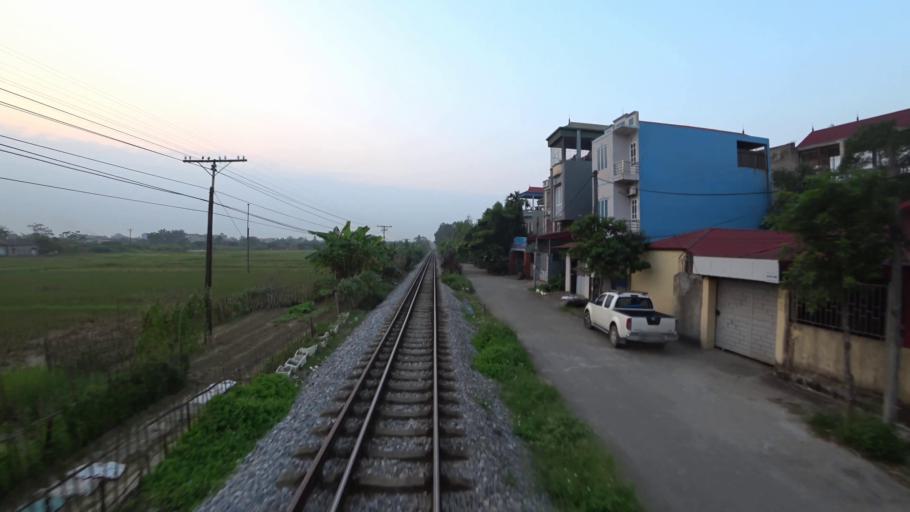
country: VN
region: Ha Noi
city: Dong Anh
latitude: 21.1490
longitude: 105.8573
